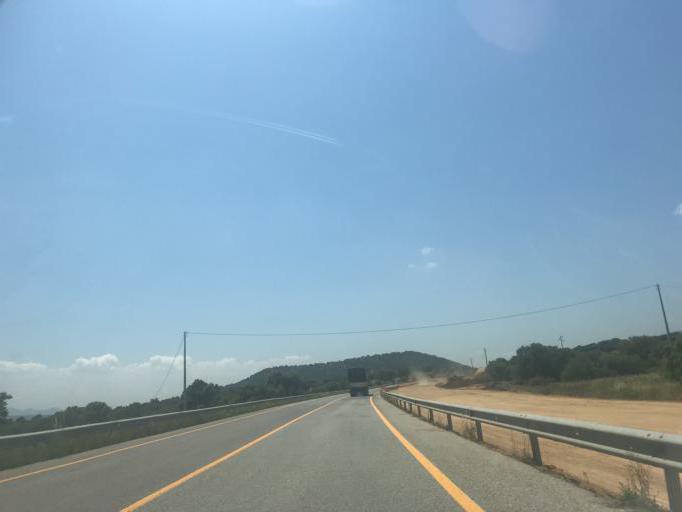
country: IT
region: Sardinia
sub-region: Provincia di Olbia-Tempio
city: Berchidda
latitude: 40.7796
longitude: 9.2420
